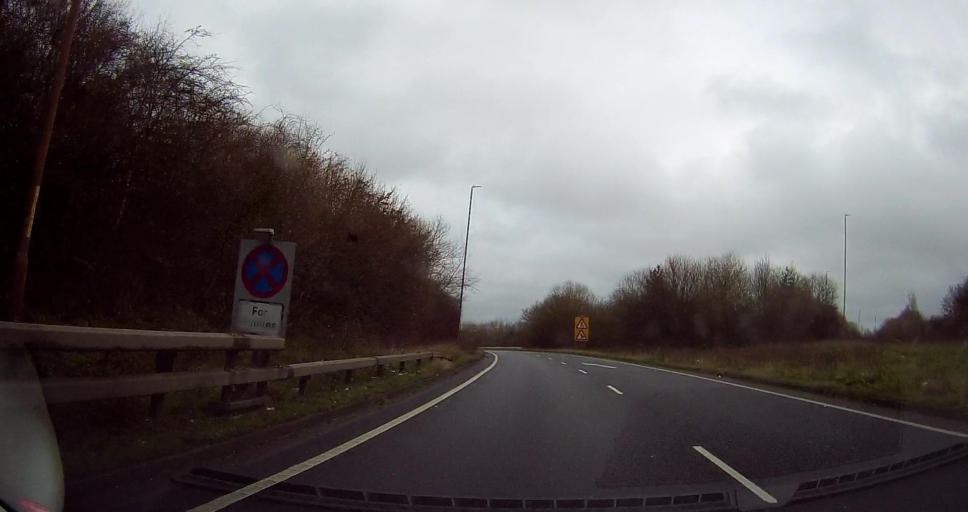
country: GB
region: England
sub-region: Medway
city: Cuxton
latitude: 51.4004
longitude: 0.4433
